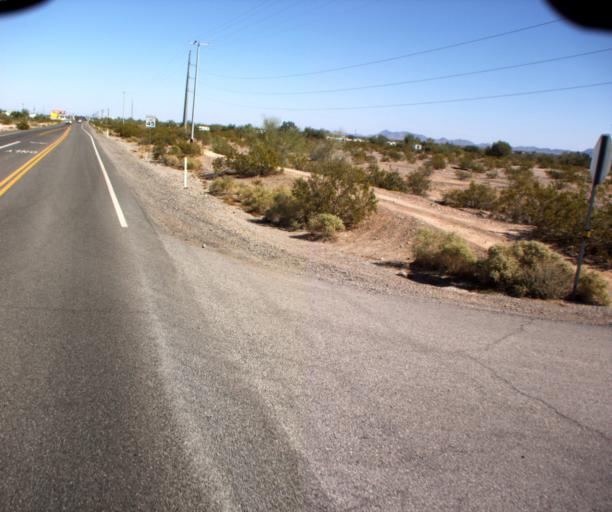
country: US
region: Arizona
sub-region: La Paz County
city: Quartzsite
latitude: 33.6517
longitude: -114.2171
